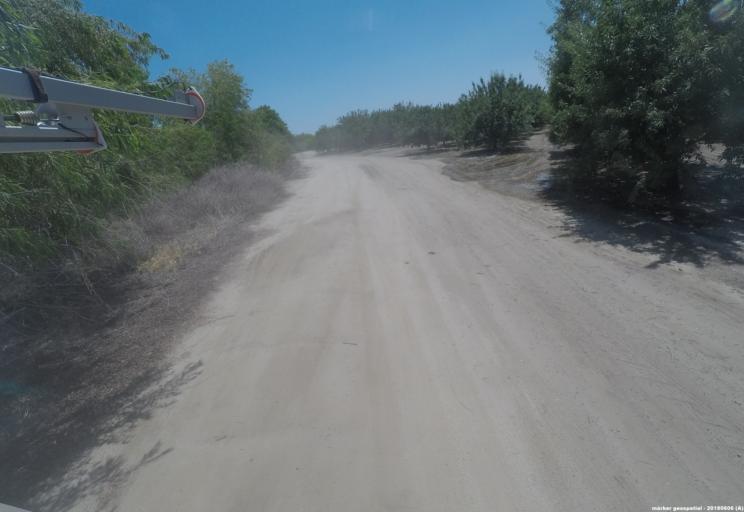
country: US
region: California
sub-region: Fresno County
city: Mendota
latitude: 36.7811
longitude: -120.2957
